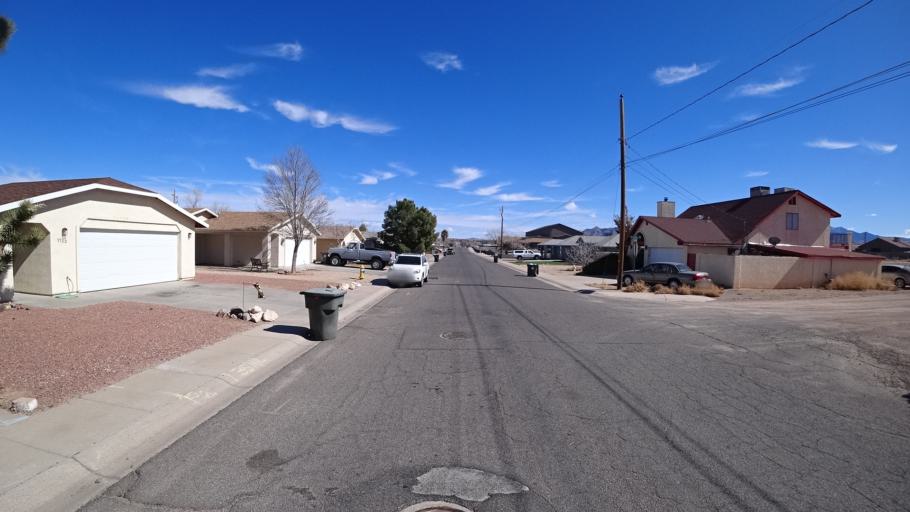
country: US
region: Arizona
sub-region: Mohave County
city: Kingman
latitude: 35.2059
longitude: -114.0379
